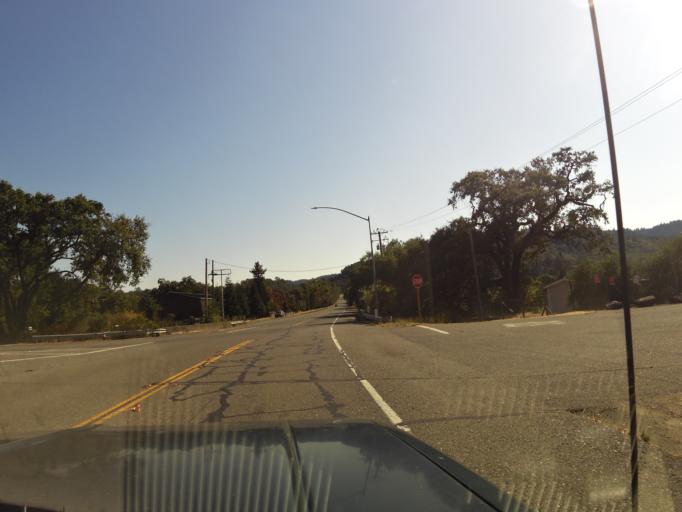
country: US
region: California
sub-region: Sonoma County
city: Cloverdale
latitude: 38.8262
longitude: -123.0161
